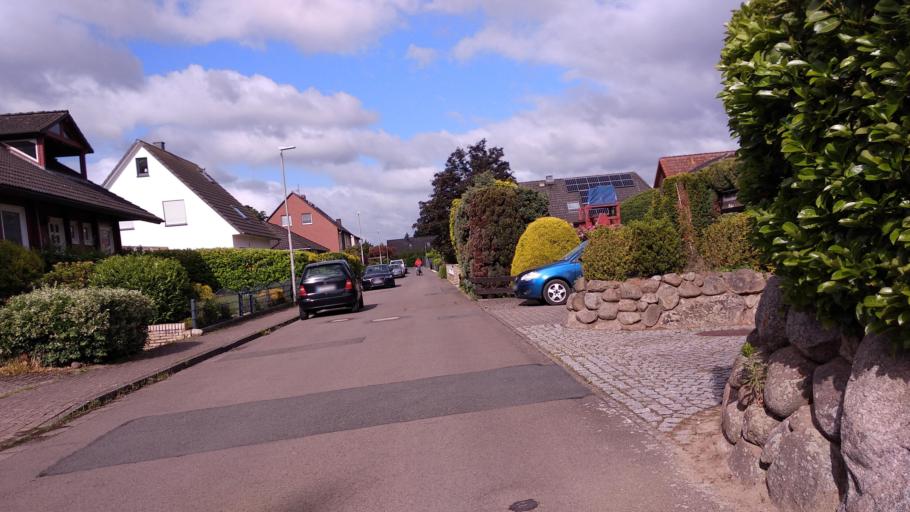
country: DE
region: Lower Saxony
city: Hagenburg
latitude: 52.4570
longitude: 9.3768
